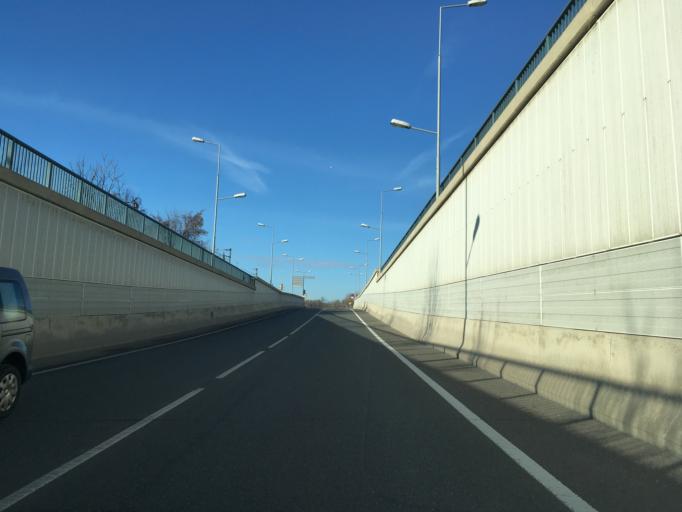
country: AT
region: Lower Austria
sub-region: Politischer Bezirk Wien-Umgebung
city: Klosterneuburg
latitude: 48.3108
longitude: 16.3259
